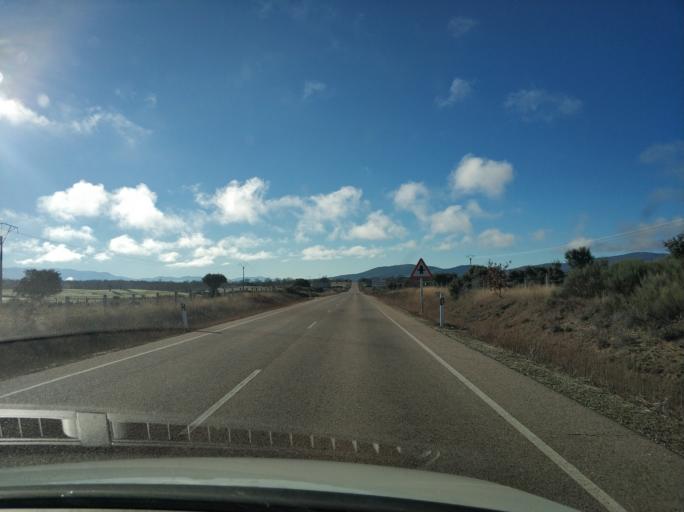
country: ES
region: Castille and Leon
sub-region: Provincia de Salamanca
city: Herguijuela del Campo
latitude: 40.6422
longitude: -5.9027
